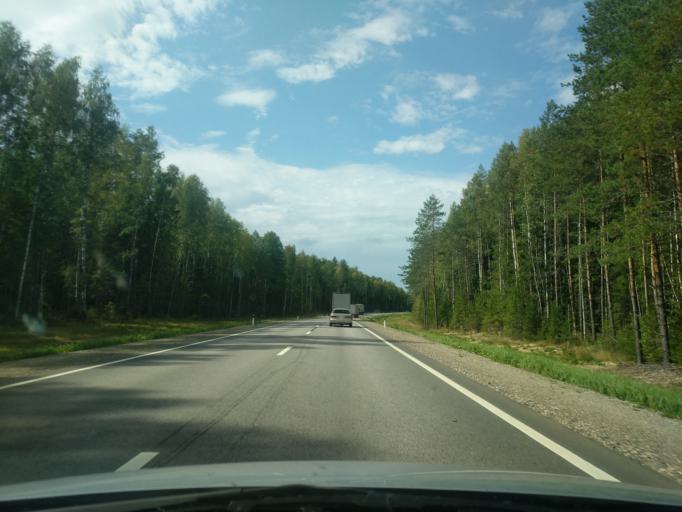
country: RU
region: Kostroma
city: Kadyy
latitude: 57.7967
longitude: 42.8466
